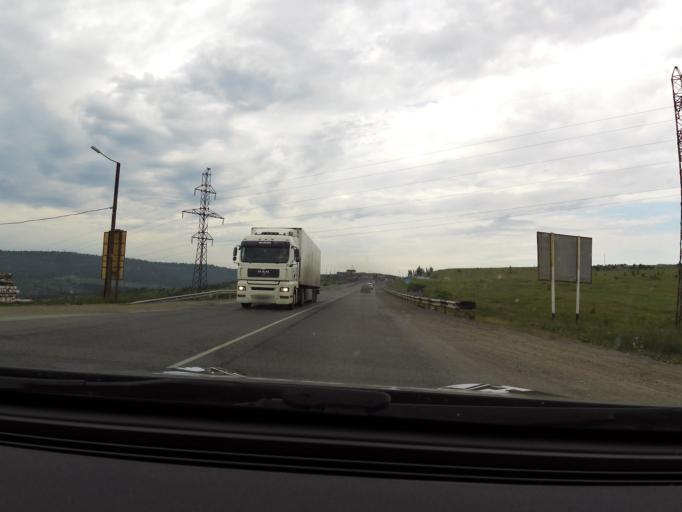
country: RU
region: Chelyabinsk
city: Sim
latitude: 55.0003
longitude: 57.6590
